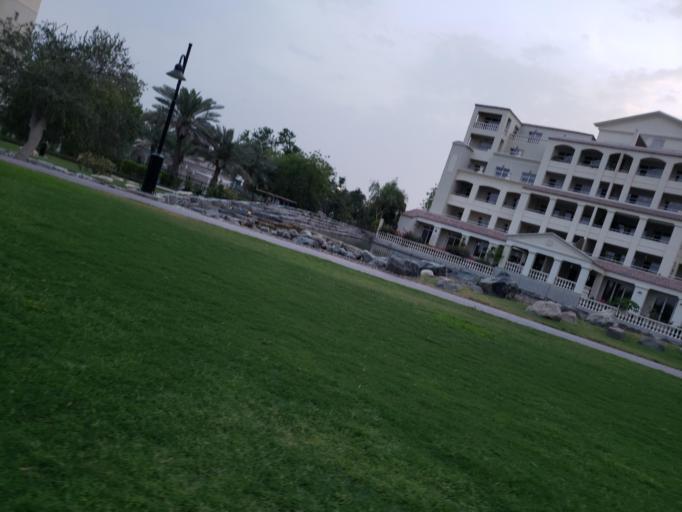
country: AE
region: Dubai
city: Dubai
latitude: 25.0400
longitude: 55.2306
